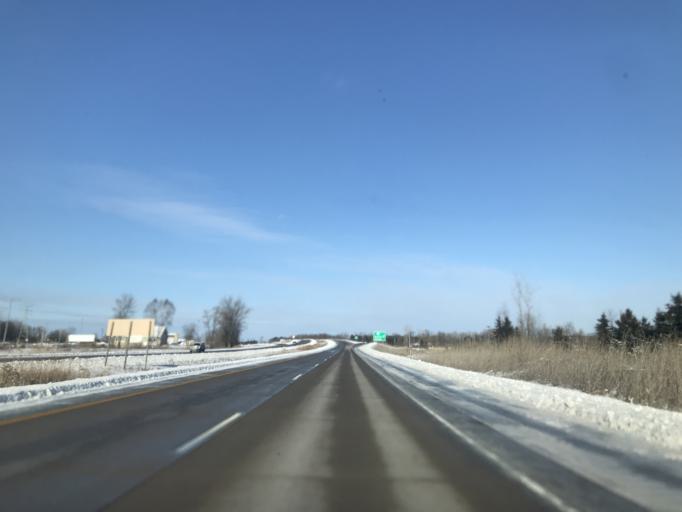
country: US
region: Wisconsin
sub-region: Oconto County
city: Oconto Falls
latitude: 44.8806
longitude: -88.0454
